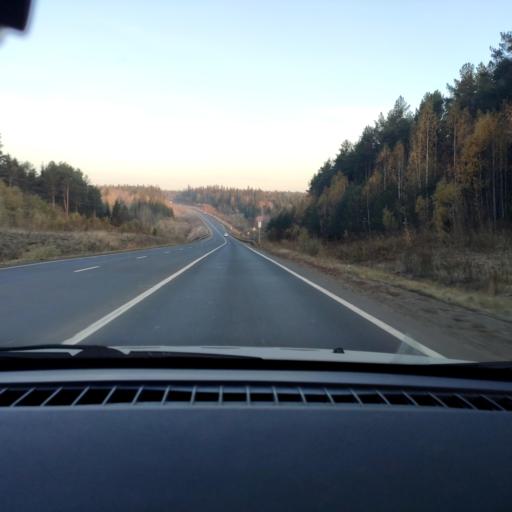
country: RU
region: Perm
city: Novyye Lyady
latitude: 58.0360
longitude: 56.4728
